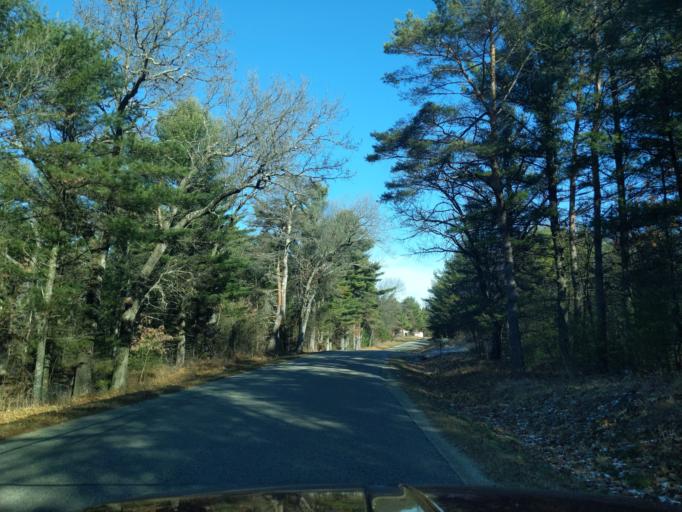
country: US
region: Wisconsin
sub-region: Waushara County
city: Silver Lake
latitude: 44.0858
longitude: -89.1939
